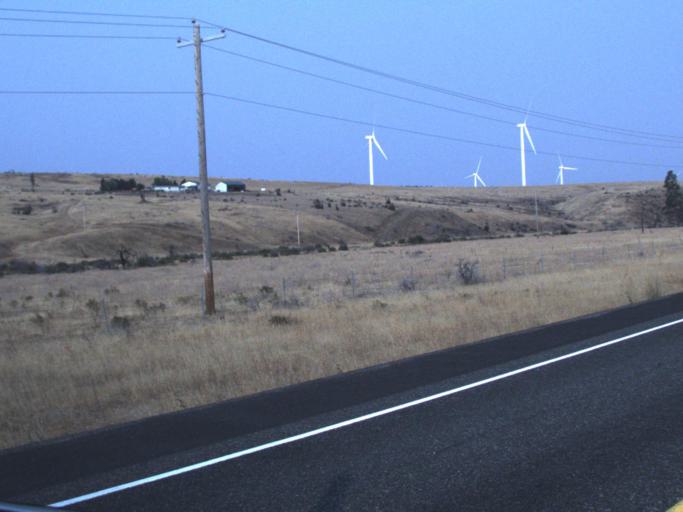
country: US
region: Washington
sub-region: Kittitas County
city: Ellensburg
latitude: 47.1229
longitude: -120.6726
